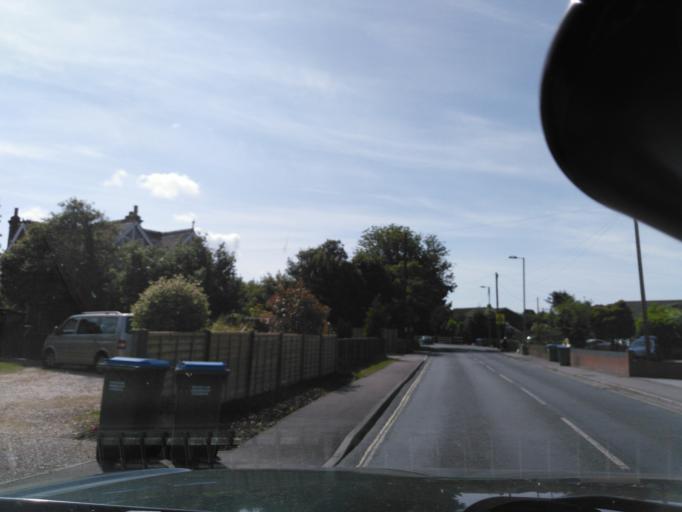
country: GB
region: England
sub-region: Hampshire
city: Lee-on-the-Solent
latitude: 50.8280
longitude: -1.2163
